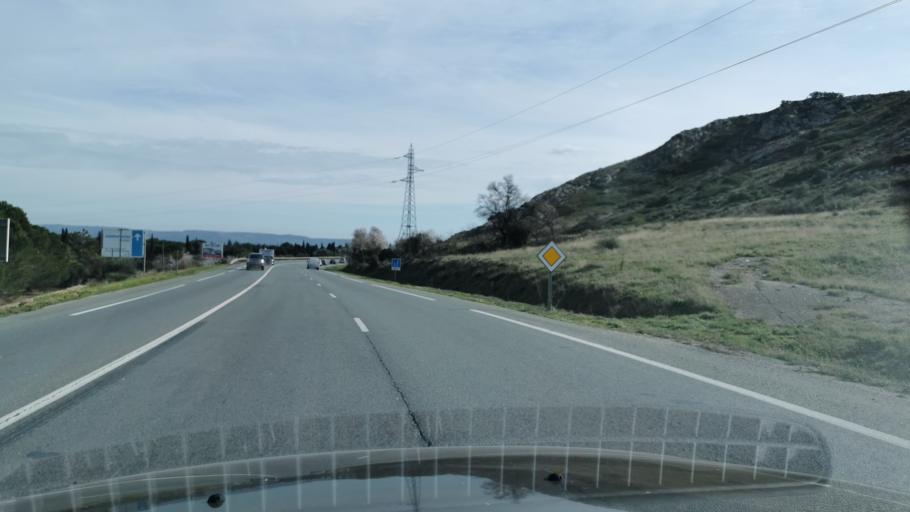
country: FR
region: Languedoc-Roussillon
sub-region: Departement de l'Aude
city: Narbonne
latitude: 43.1779
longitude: 2.9695
